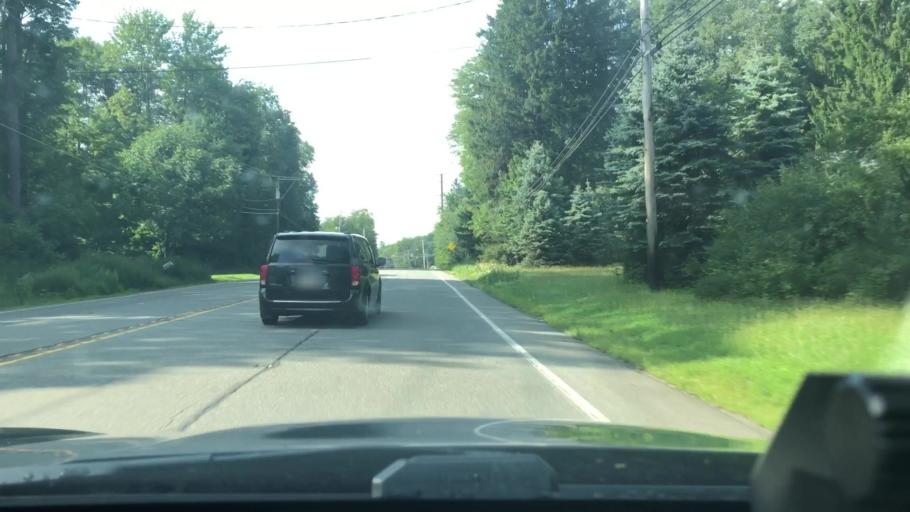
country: US
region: Pennsylvania
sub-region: Lackawanna County
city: Moscow
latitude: 41.2569
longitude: -75.5047
